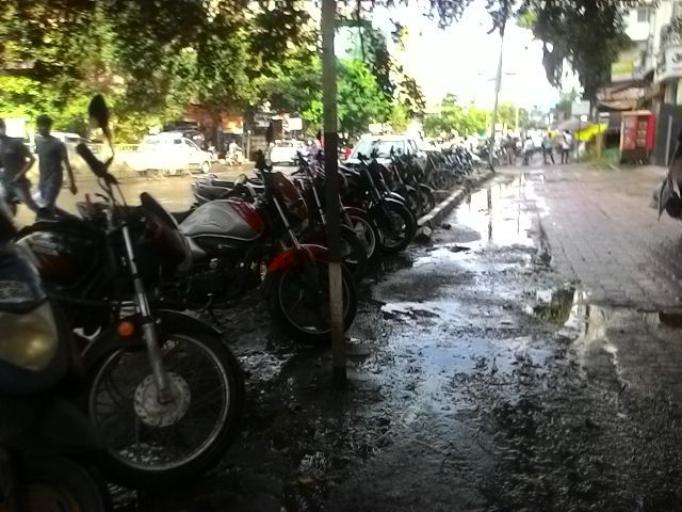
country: IN
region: Maharashtra
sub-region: Pune Division
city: Khadki
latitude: 18.5578
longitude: 73.7929
